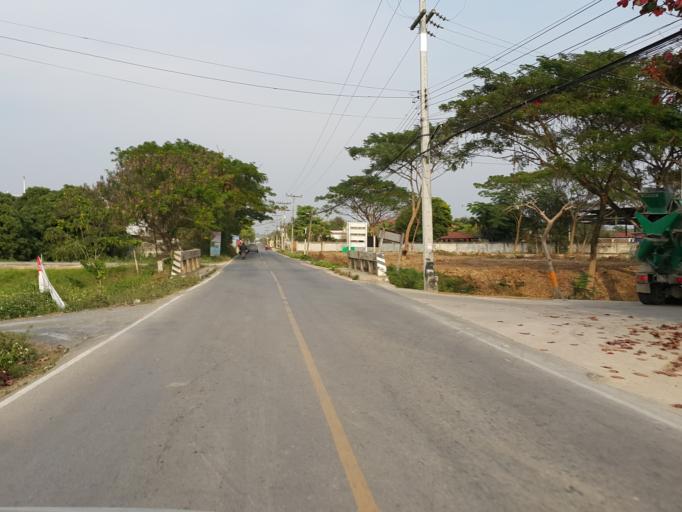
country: TH
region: Chiang Mai
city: Saraphi
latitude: 18.6969
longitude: 99.0118
